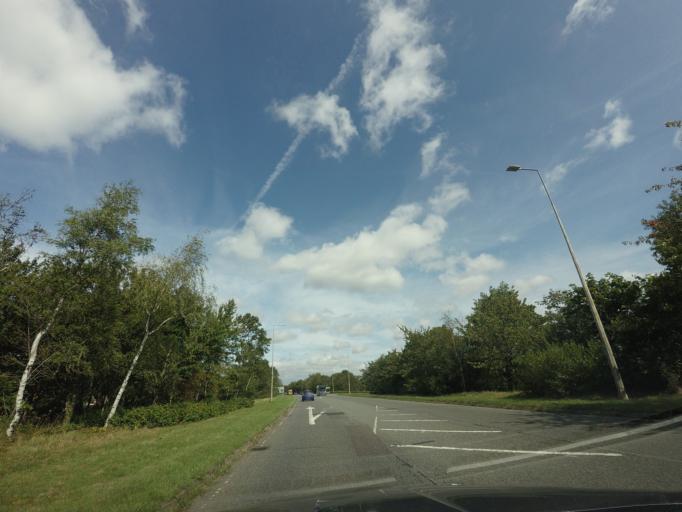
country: GB
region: England
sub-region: Milton Keynes
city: Simpson
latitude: 52.0088
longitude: -0.6941
